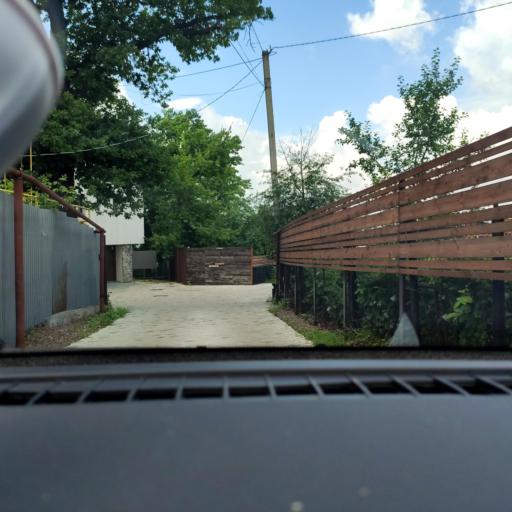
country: RU
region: Samara
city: Samara
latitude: 53.2736
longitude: 50.1870
